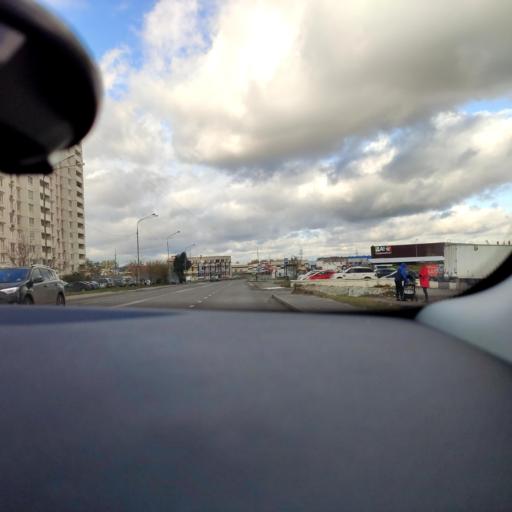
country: RU
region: Moskovskaya
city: Kotel'niki
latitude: 55.6380
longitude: 37.8467
